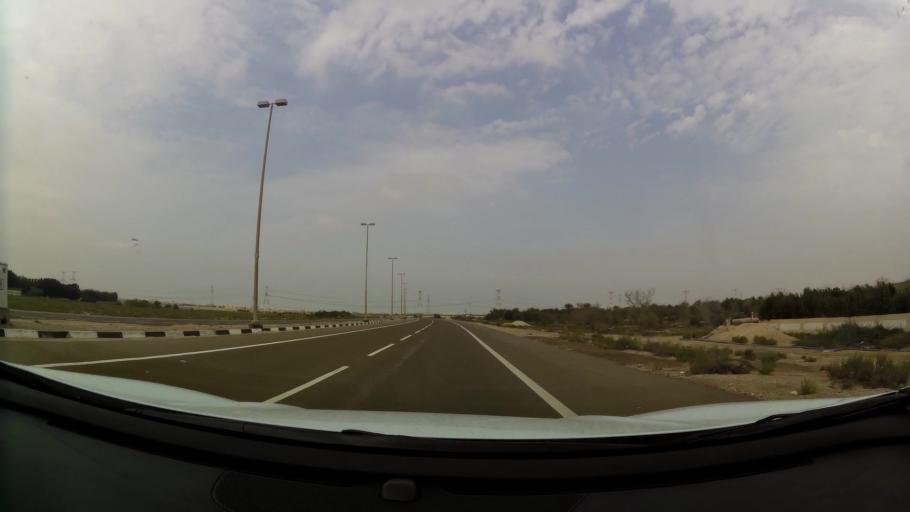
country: AE
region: Abu Dhabi
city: Abu Dhabi
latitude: 24.6307
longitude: 54.7042
